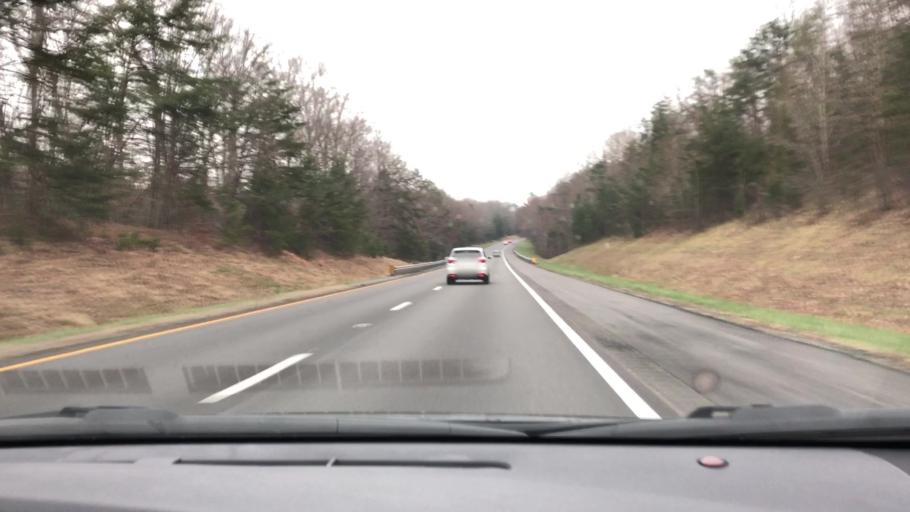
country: US
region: Virginia
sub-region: Fluvanna County
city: Lake Monticello
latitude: 37.9942
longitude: -78.2600
